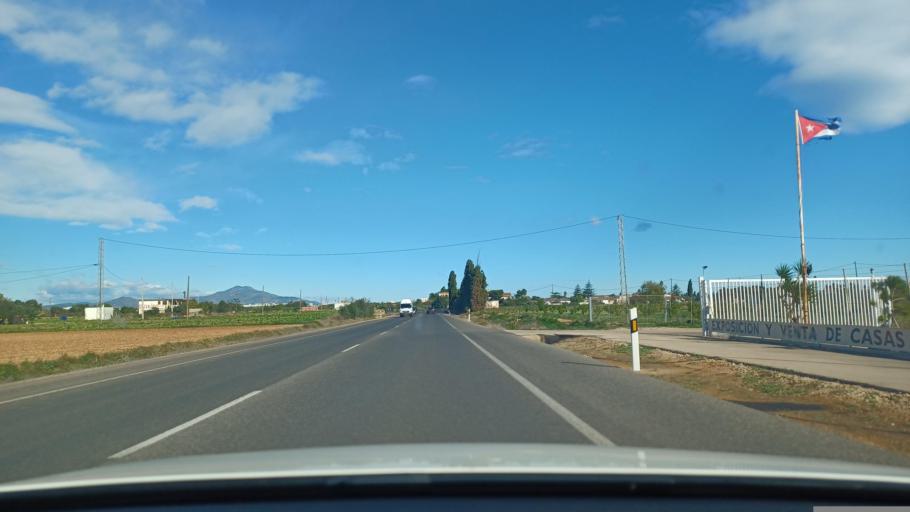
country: ES
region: Valencia
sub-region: Provincia de Castello
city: Benicarlo
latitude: 40.4437
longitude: 0.4458
